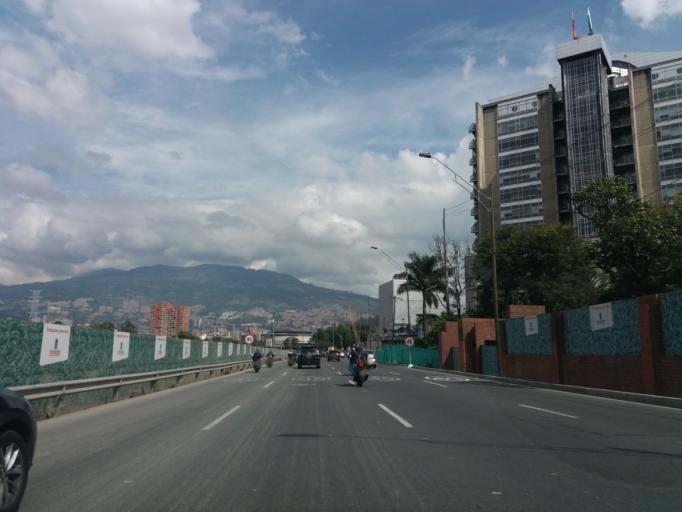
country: CO
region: Antioquia
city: Medellin
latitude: 6.2437
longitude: -75.5782
